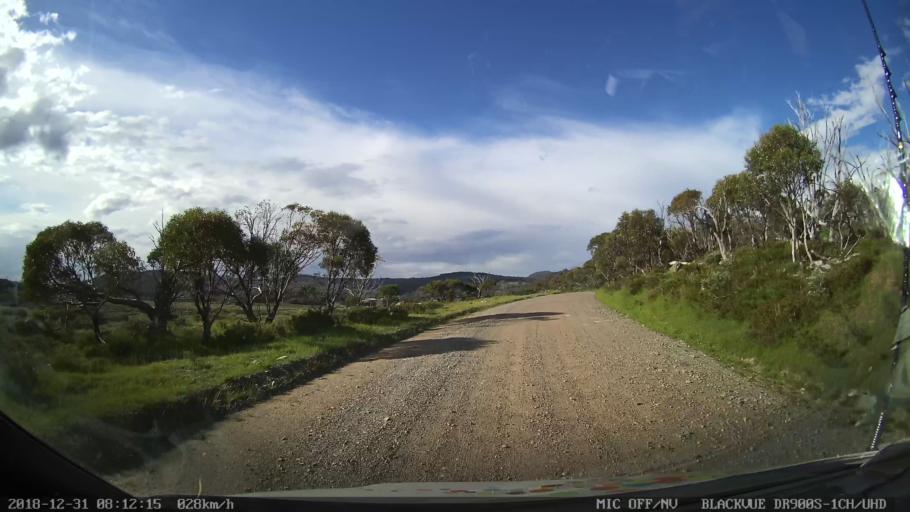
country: AU
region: New South Wales
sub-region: Snowy River
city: Jindabyne
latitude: -36.3866
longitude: 148.4302
